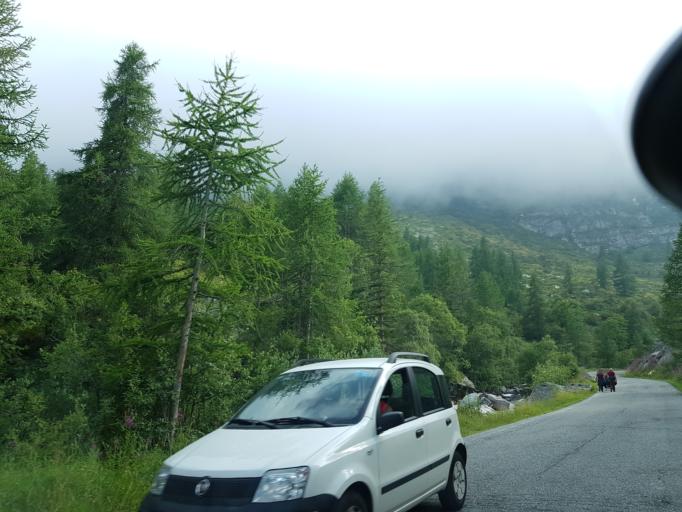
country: IT
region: Piedmont
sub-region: Provincia di Cuneo
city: Pleyne
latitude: 44.5739
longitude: 6.9899
